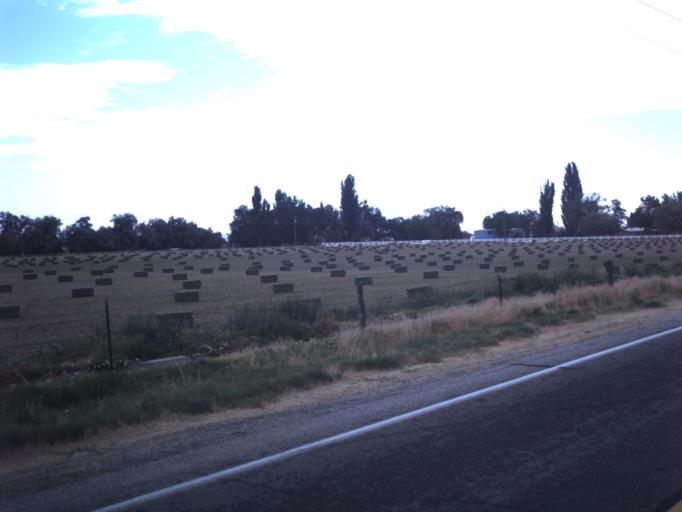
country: US
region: Utah
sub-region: Davis County
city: West Point
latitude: 41.0940
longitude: -112.1127
